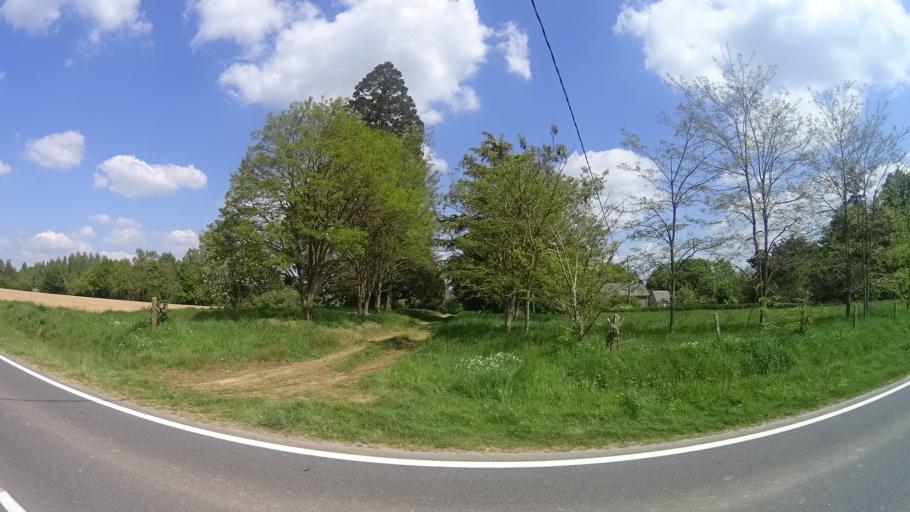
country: FR
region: Brittany
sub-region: Departement du Morbihan
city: Rieux
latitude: 47.6088
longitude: -2.1109
